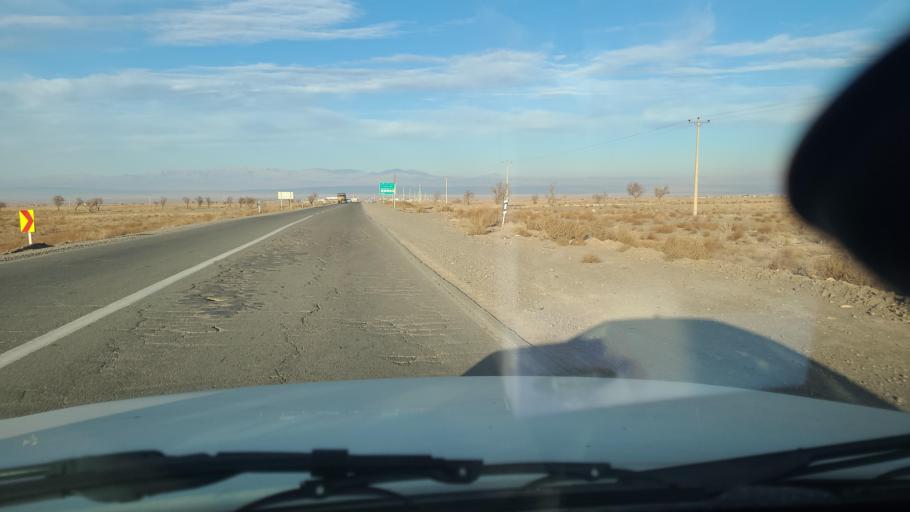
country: IR
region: Razavi Khorasan
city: Neqab
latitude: 36.5010
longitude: 57.5315
